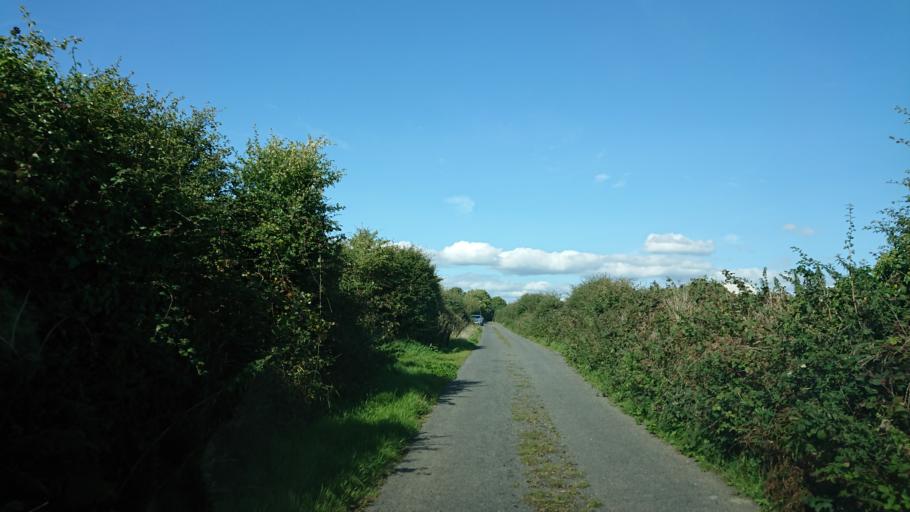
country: IE
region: Munster
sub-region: Waterford
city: Waterford
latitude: 52.2075
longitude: -7.0564
